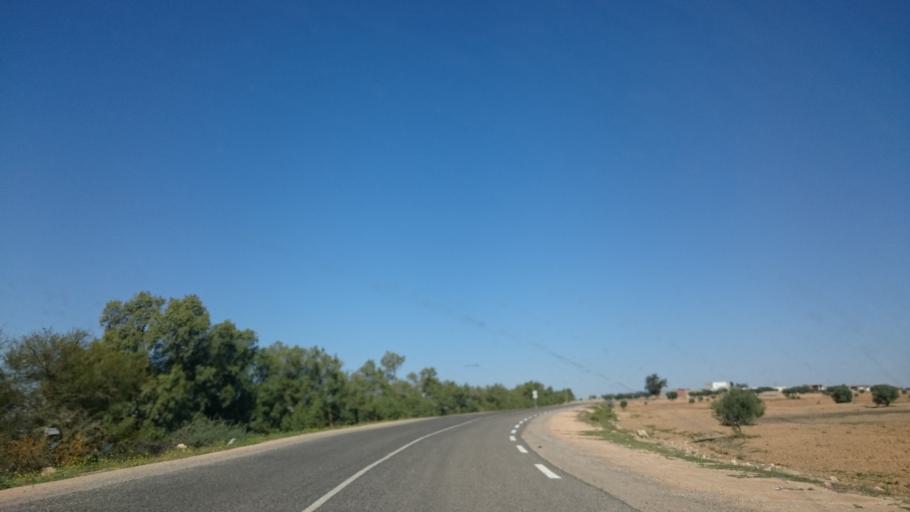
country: TN
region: Safaqis
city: Sfax
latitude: 34.7594
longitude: 10.5177
